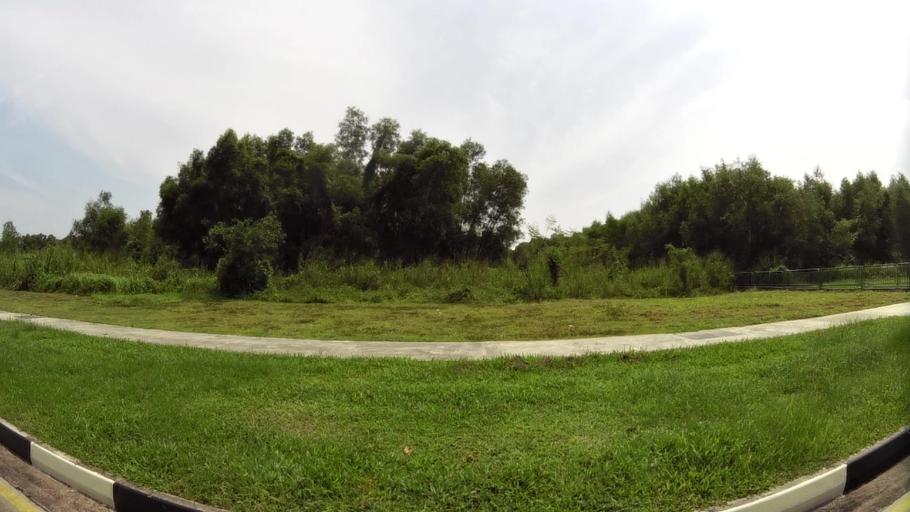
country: MY
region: Johor
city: Kampung Pasir Gudang Baru
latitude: 1.3769
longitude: 103.9618
